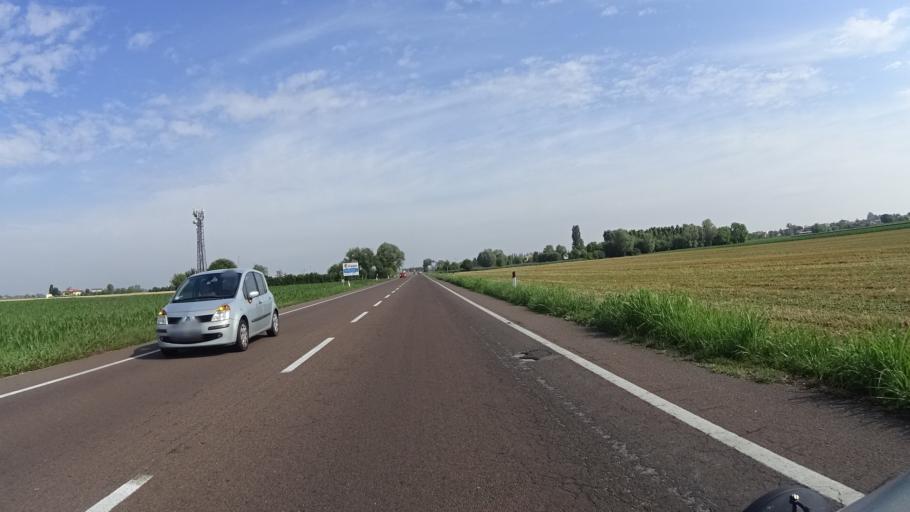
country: IT
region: Veneto
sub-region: Provincia di Venezia
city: San Michele al Tagliamento
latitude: 45.7543
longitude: 12.9882
